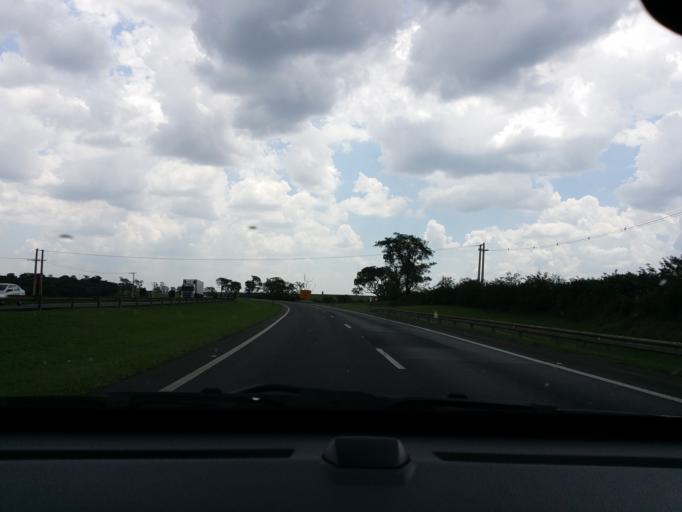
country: BR
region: Sao Paulo
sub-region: Itirapina
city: Itirapina
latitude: -22.2484
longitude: -47.7048
